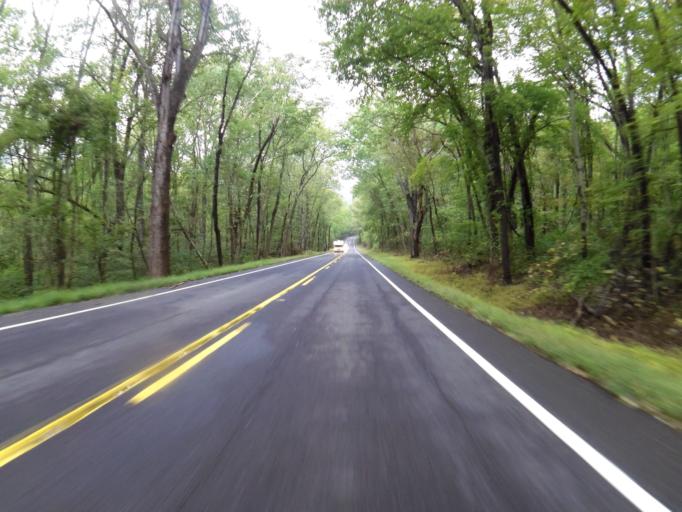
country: US
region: Virginia
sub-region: Rappahannock County
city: Washington
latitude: 38.6567
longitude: -78.2779
